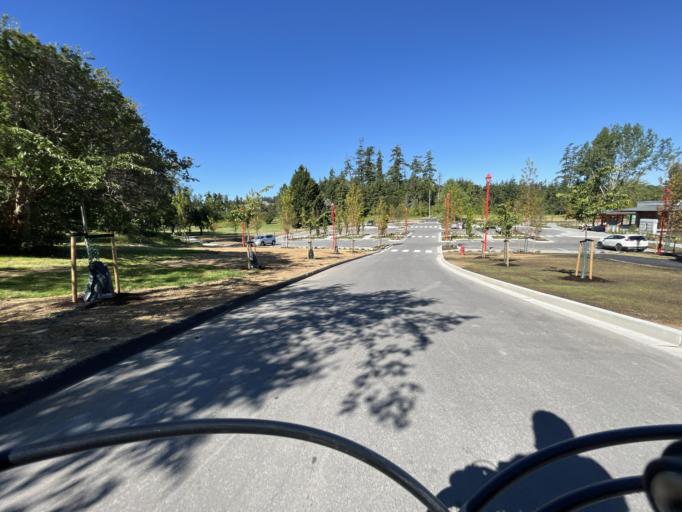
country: CA
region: British Columbia
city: Victoria
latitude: 48.4462
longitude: -123.4040
